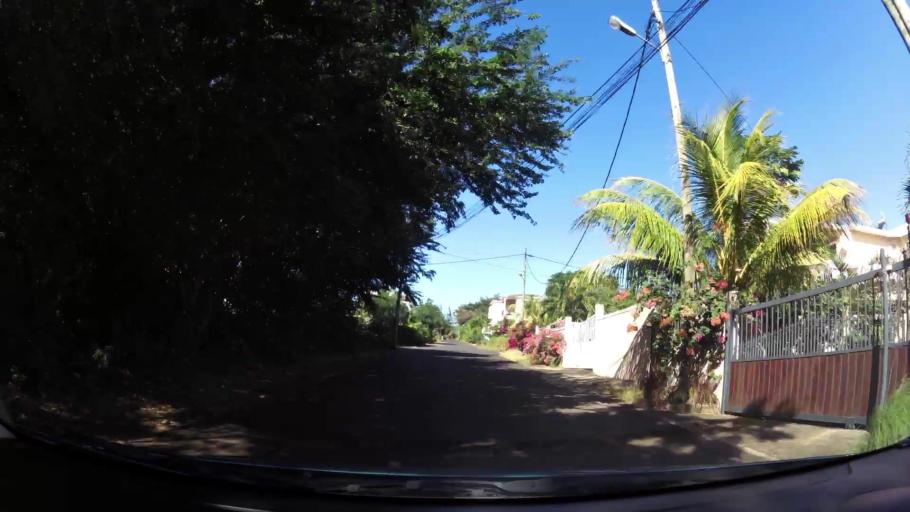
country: MU
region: Black River
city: Albion
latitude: -20.2184
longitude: 57.4030
